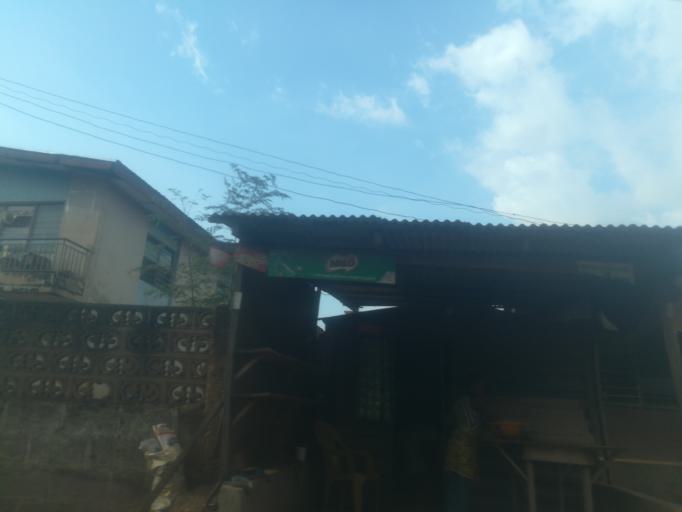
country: NG
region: Ogun
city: Abeokuta
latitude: 7.1487
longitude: 3.3105
